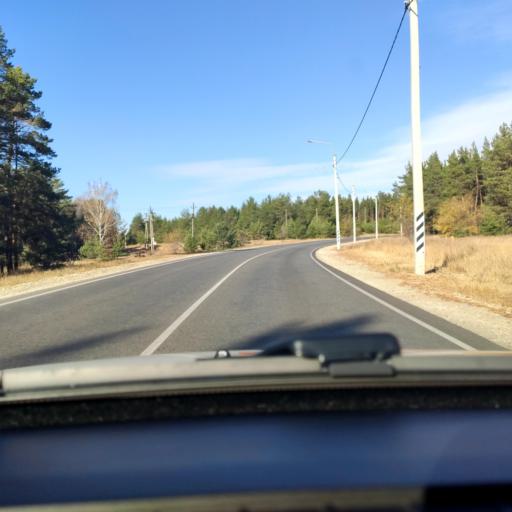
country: RU
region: Voronezj
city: Shilovo
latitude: 51.5285
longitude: 39.1421
